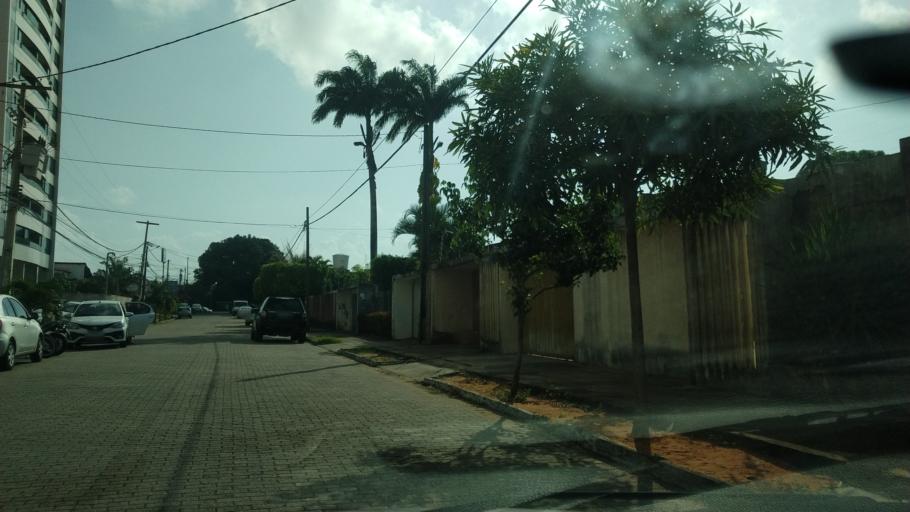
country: BR
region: Rio Grande do Norte
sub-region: Natal
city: Natal
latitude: -5.8563
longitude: -35.2007
